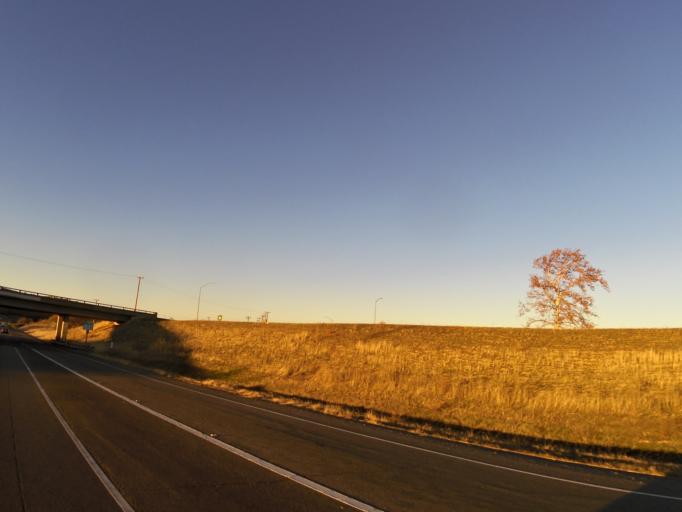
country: US
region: California
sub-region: San Luis Obispo County
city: San Miguel
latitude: 35.8147
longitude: -120.7543
